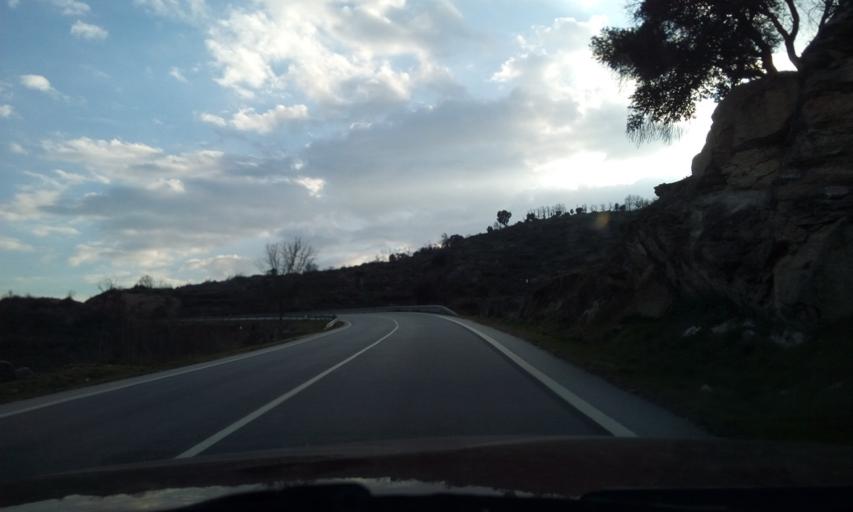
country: ES
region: Castille and Leon
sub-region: Provincia de Salamanca
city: Aldea del Obispo
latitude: 40.7012
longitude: -6.9331
